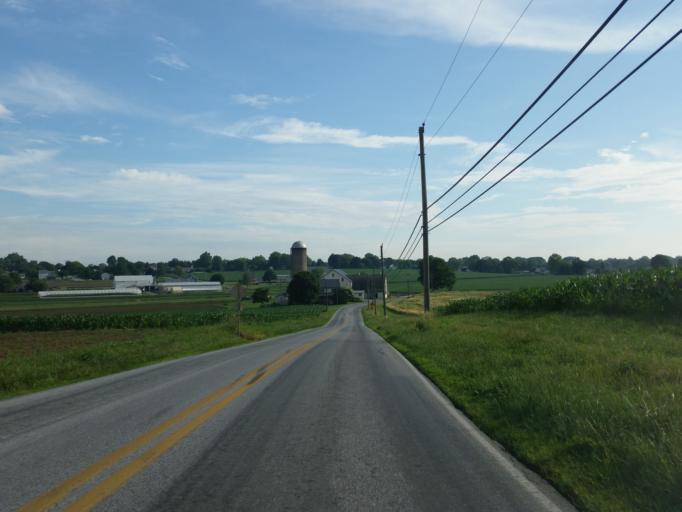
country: US
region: Pennsylvania
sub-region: Lancaster County
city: Strasburg
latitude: 39.9690
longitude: -76.1814
